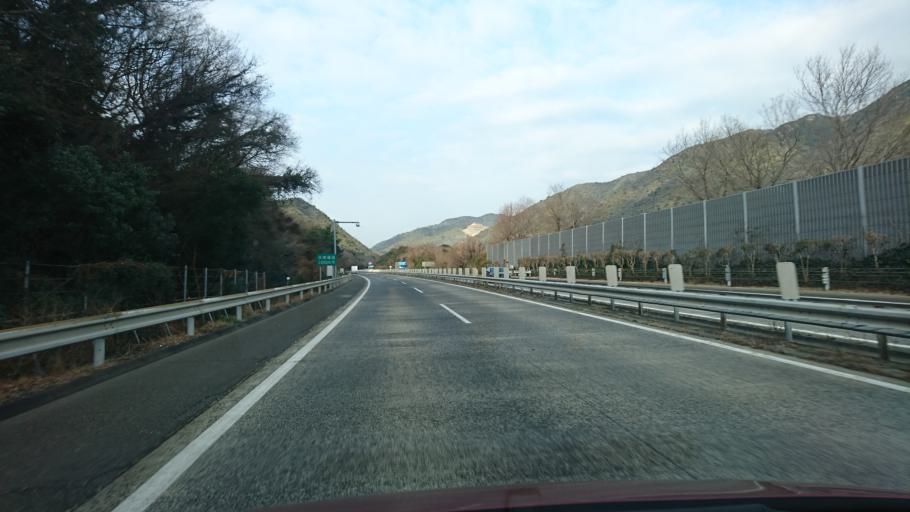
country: JP
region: Hyogo
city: Kariya
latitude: 34.7763
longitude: 134.3545
